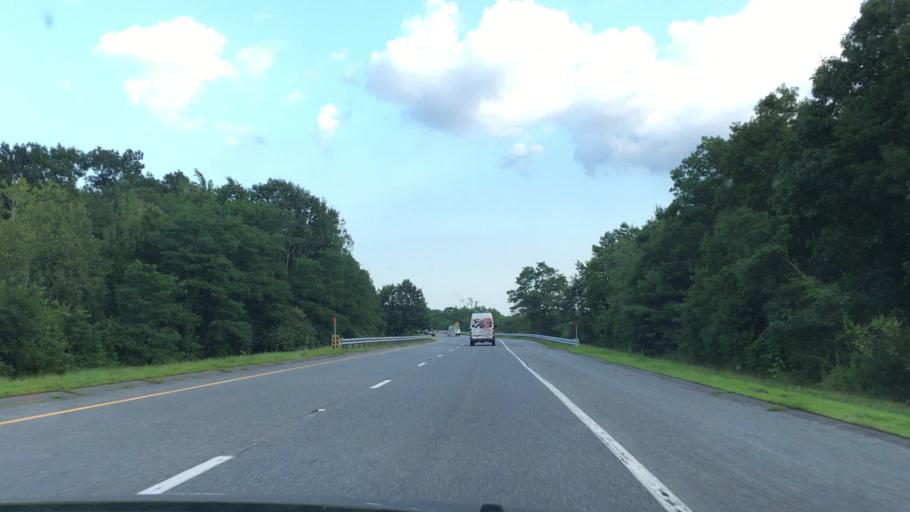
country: US
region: Massachusetts
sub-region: Essex County
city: South Peabody
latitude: 42.5279
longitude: -70.9797
